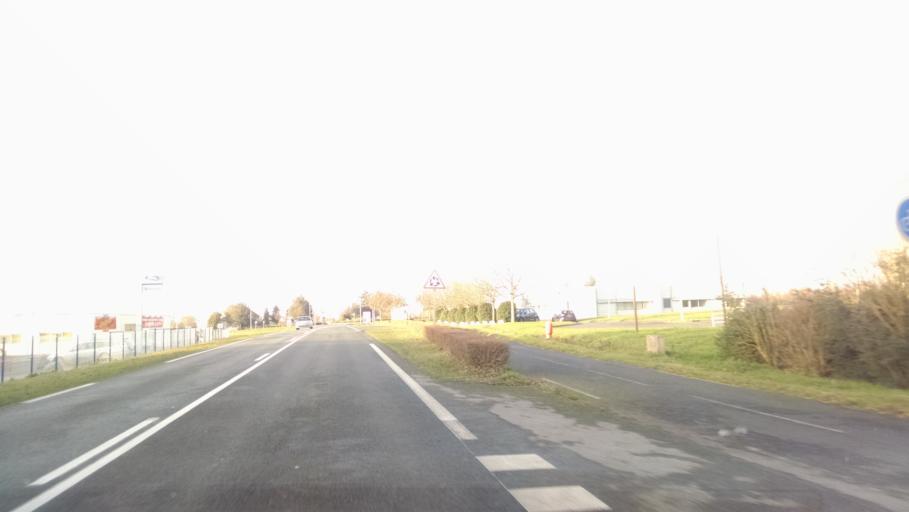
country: FR
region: Pays de la Loire
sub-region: Departement de la Vendee
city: Saint-Hilaire-de-Loulay
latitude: 46.9947
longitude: -1.3267
